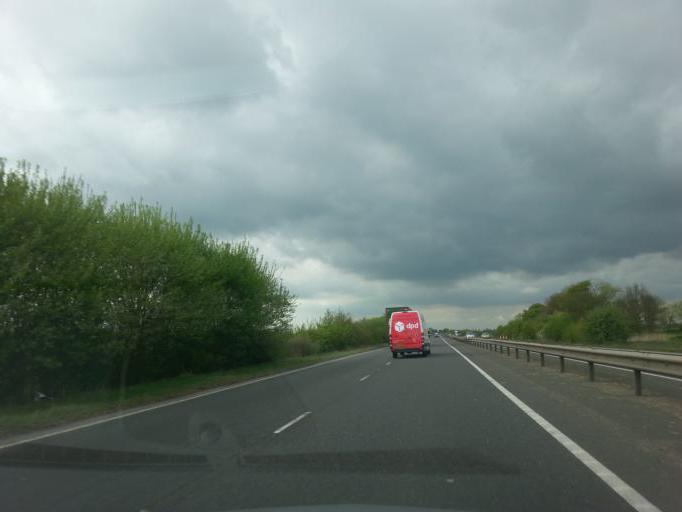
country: GB
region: England
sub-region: Peterborough
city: Thorney
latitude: 52.6224
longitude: -0.0712
